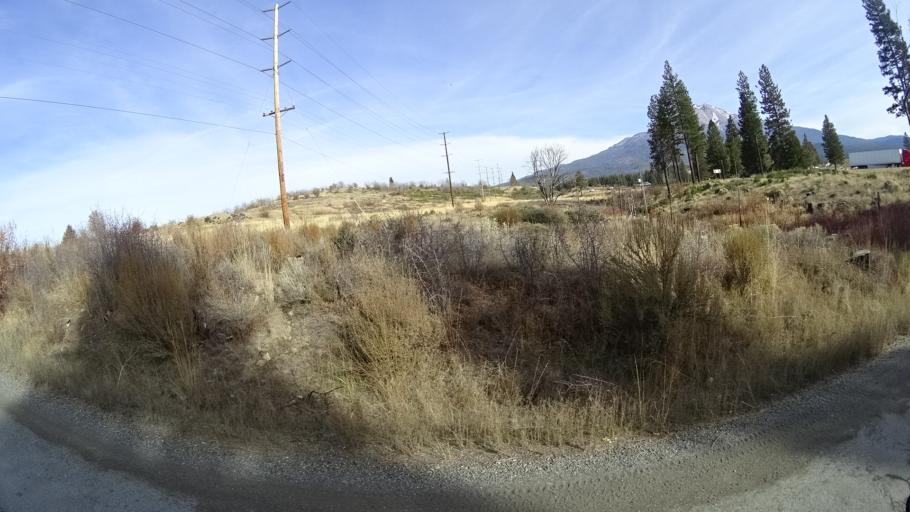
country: US
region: California
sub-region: Siskiyou County
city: Weed
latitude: 41.4412
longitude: -122.3866
